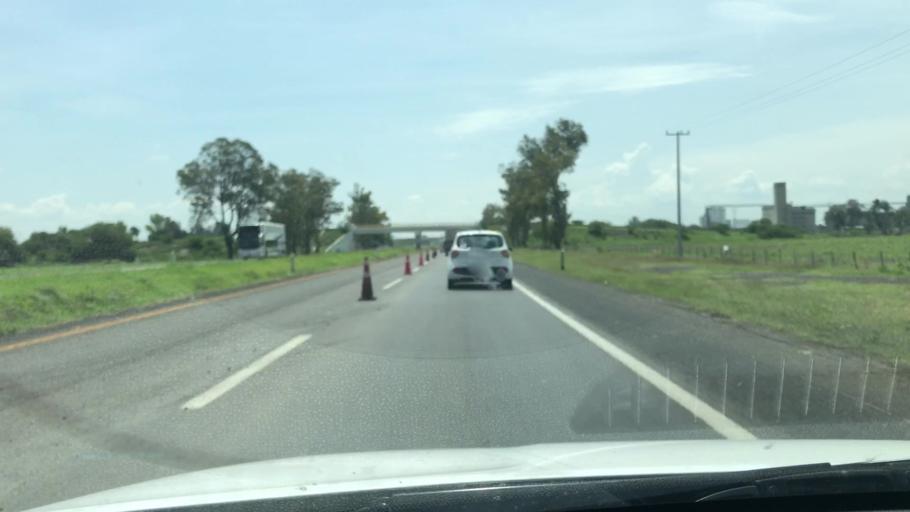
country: MX
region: Jalisco
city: La Barca
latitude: 20.3220
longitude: -102.5435
